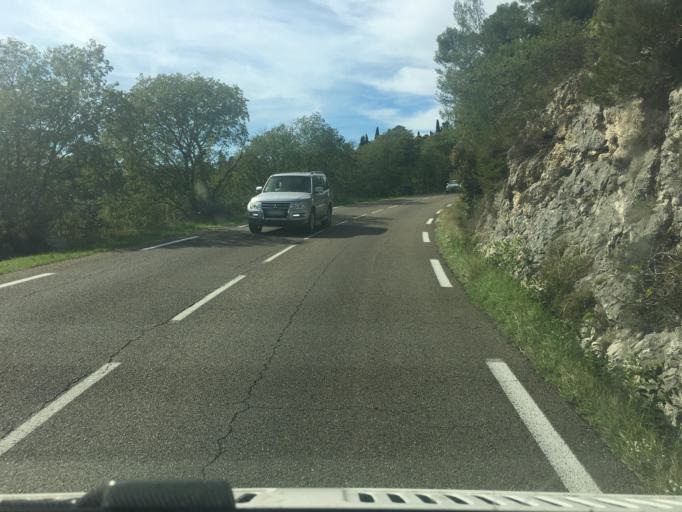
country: FR
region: Languedoc-Roussillon
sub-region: Departement du Gard
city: Uzes
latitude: 44.0154
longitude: 4.4277
